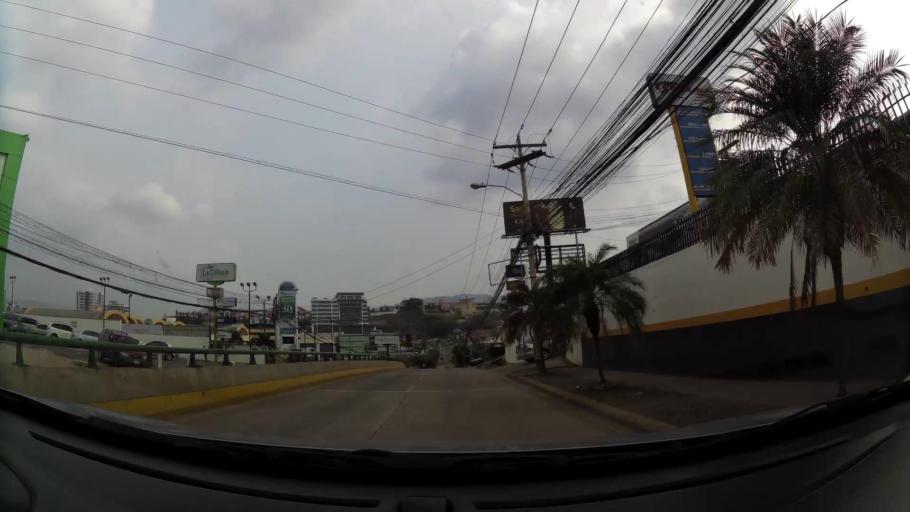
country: HN
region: Francisco Morazan
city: Tegucigalpa
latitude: 14.0854
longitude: -87.1738
